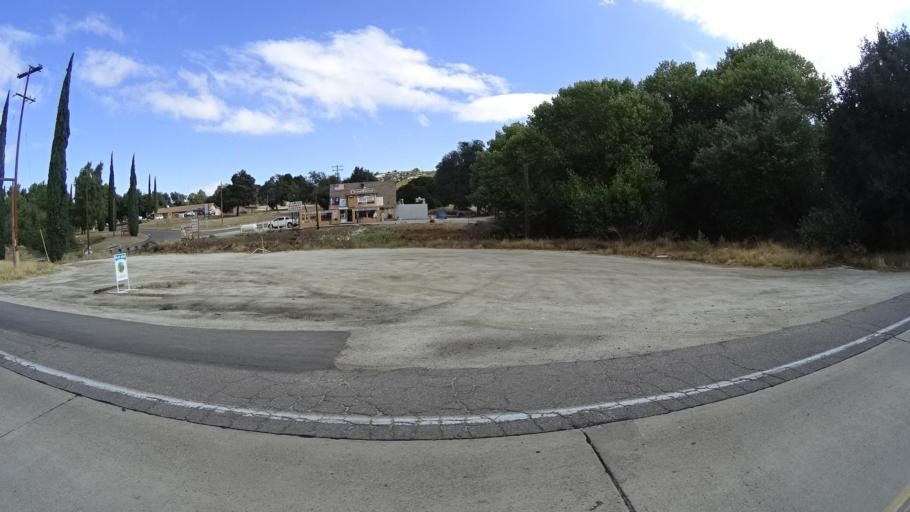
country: US
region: California
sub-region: San Diego County
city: Campo
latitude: 32.6868
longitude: -116.3361
